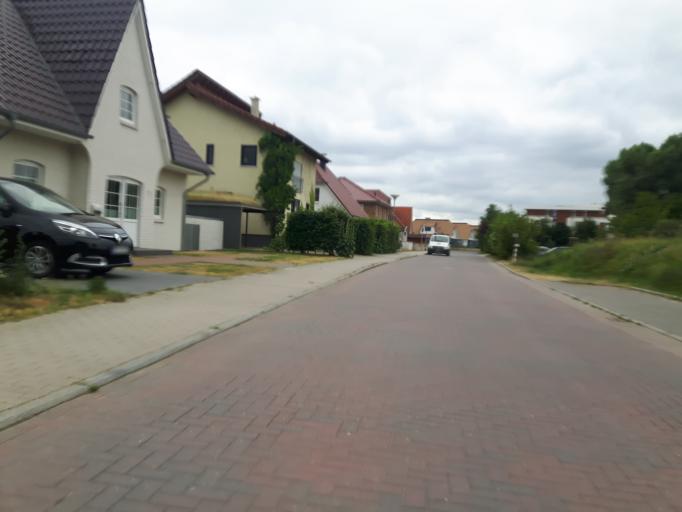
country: DE
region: Schleswig-Holstein
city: Schashagen
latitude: 54.0889
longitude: 10.8646
